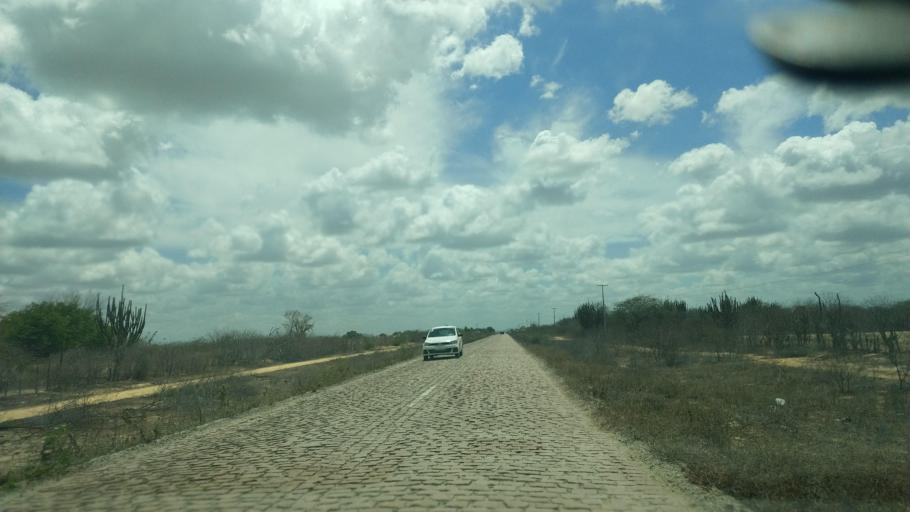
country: BR
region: Rio Grande do Norte
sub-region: Sao Paulo Do Potengi
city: Sao Paulo do Potengi
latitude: -5.9728
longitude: -35.8544
